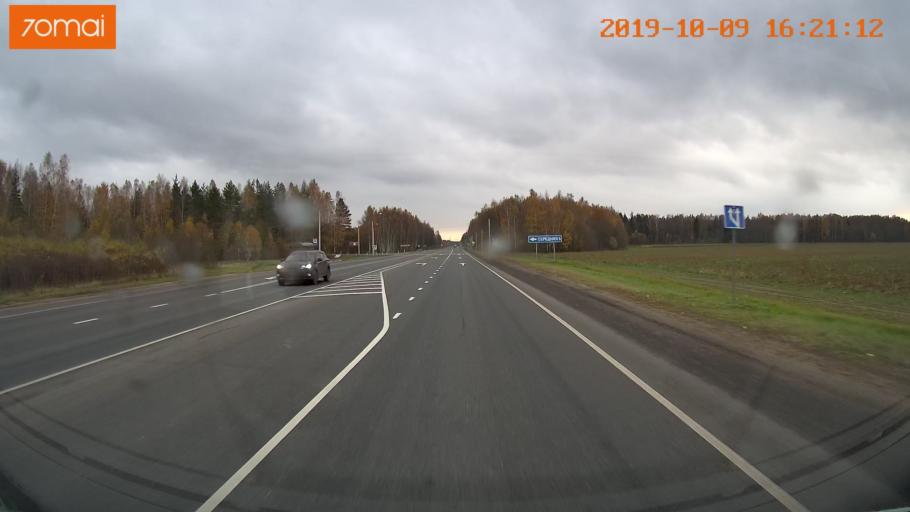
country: RU
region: Kostroma
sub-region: Kostromskoy Rayon
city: Kostroma
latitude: 57.6956
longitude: 40.8899
